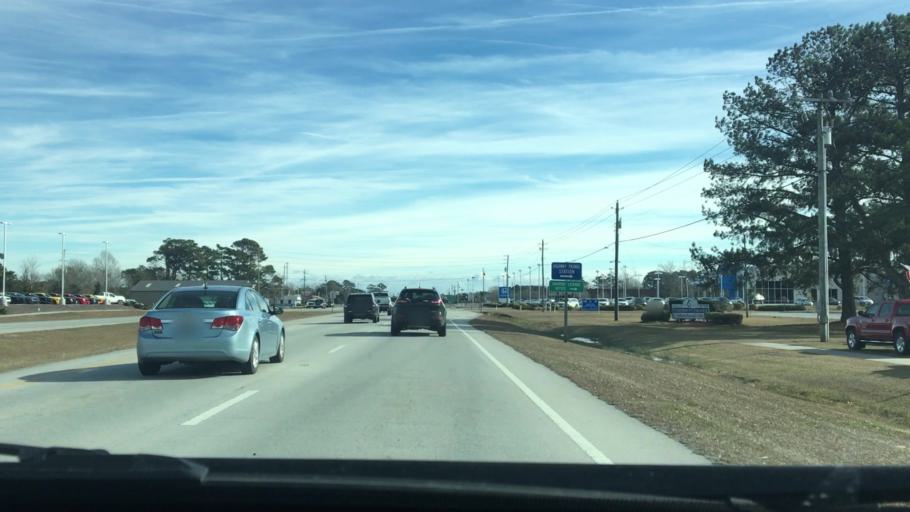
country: US
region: North Carolina
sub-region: Carteret County
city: Pine Knoll Shores
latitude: 34.7426
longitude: -76.8220
